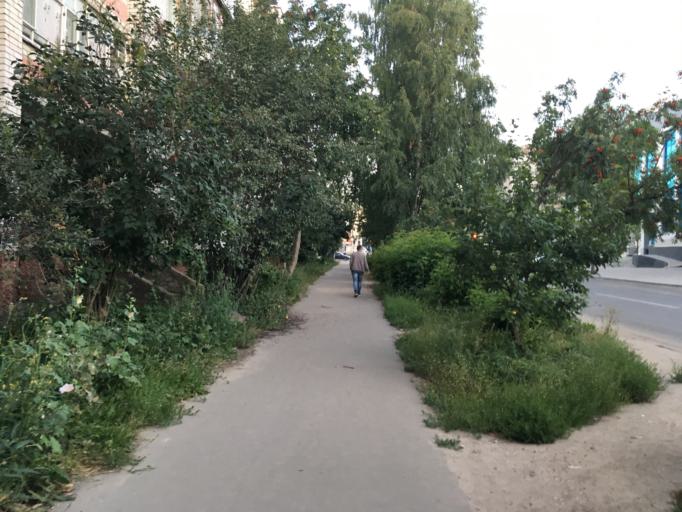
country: RU
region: Mariy-El
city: Yoshkar-Ola
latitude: 56.6471
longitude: 47.8645
